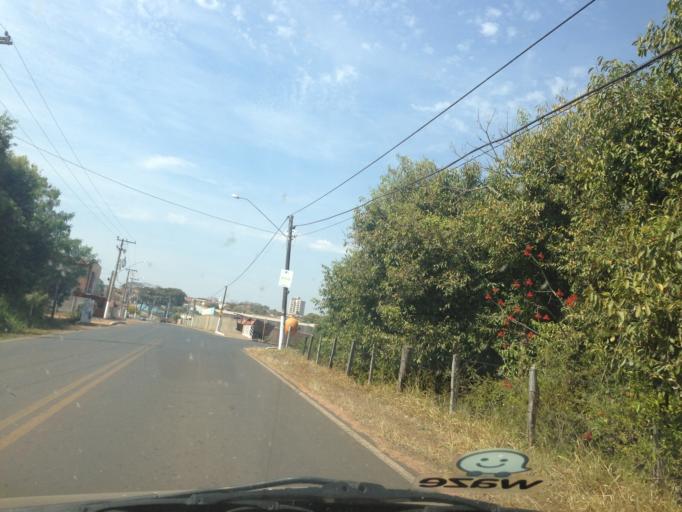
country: BR
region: Sao Paulo
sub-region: Casa Branca
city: Casa Branca
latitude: -21.7697
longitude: -47.0945
